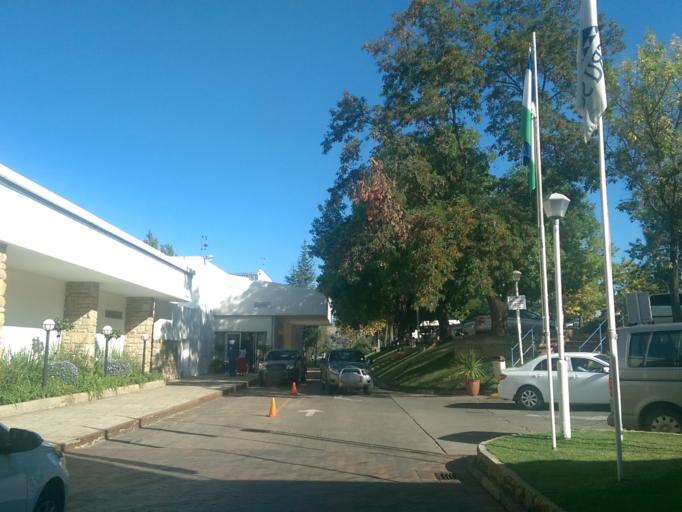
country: LS
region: Maseru
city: Maseru
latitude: -29.3167
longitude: 27.4735
